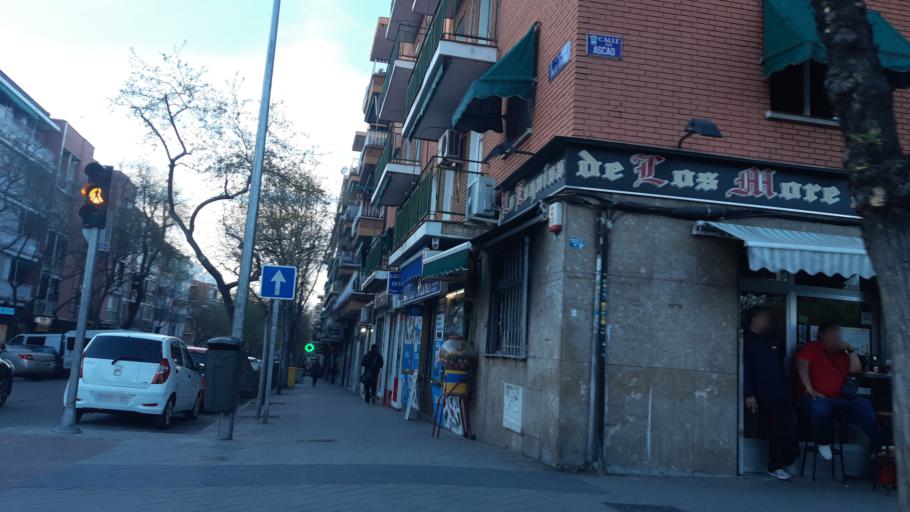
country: ES
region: Madrid
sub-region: Provincia de Madrid
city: Moratalaz
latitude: 40.4305
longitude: -3.6404
